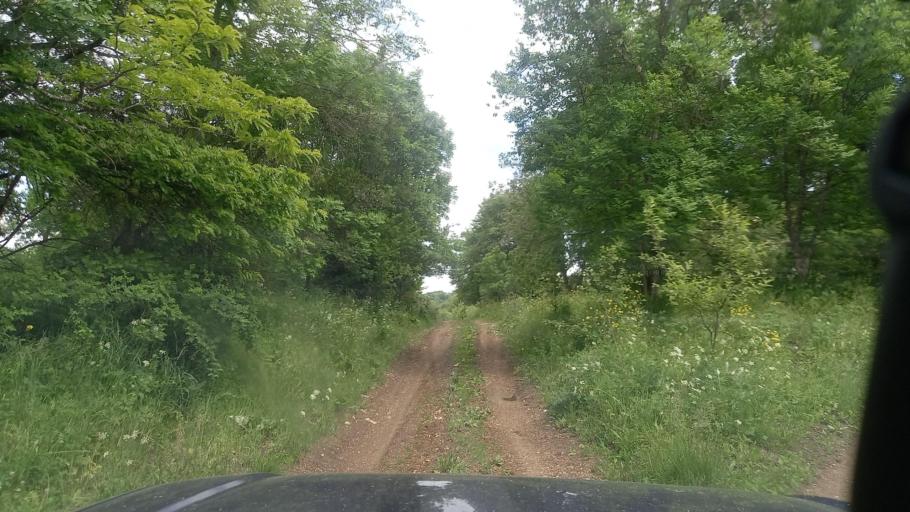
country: RU
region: Karachayevo-Cherkesiya
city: Pregradnaya
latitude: 44.0778
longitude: 41.2559
